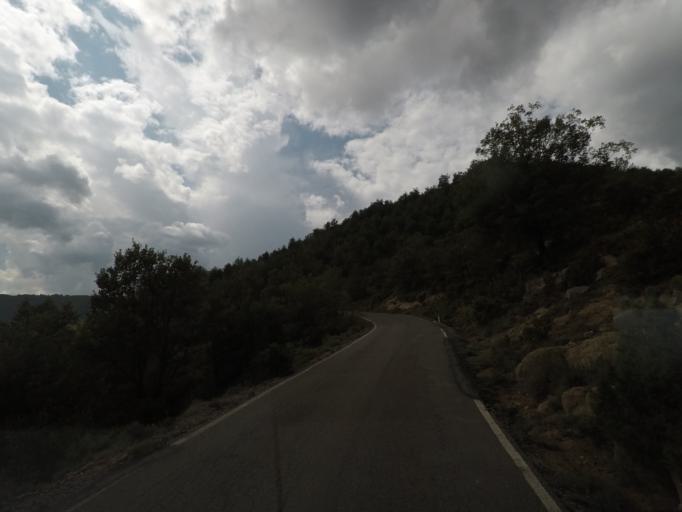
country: ES
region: Aragon
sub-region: Provincia de Huesca
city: Boltana
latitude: 42.4098
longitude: -0.0033
